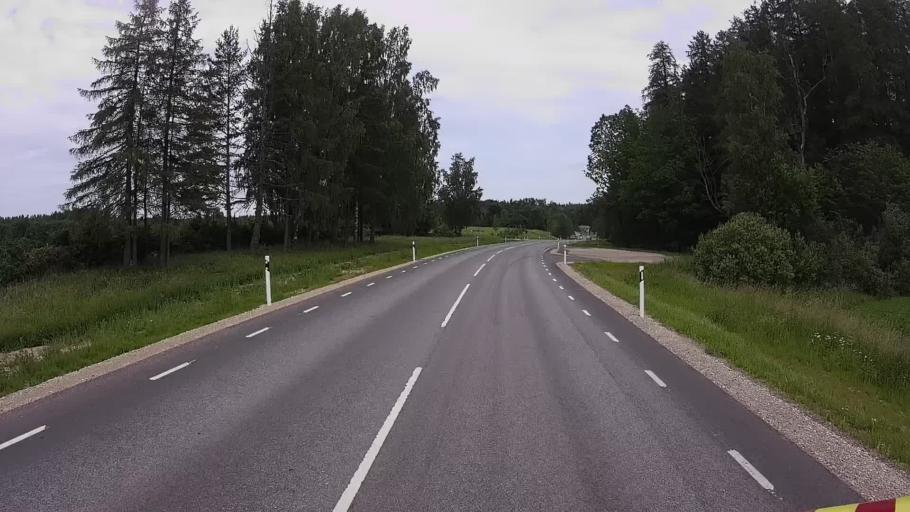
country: EE
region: Viljandimaa
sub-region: Viljandi linn
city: Viljandi
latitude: 58.2781
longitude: 25.5826
